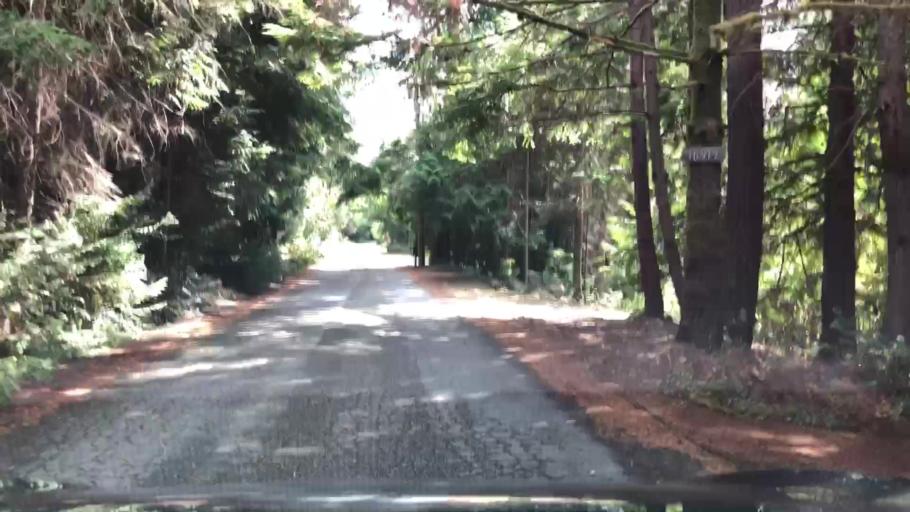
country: US
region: Washington
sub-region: King County
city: Cottage Lake
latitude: 47.7516
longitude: -122.0714
